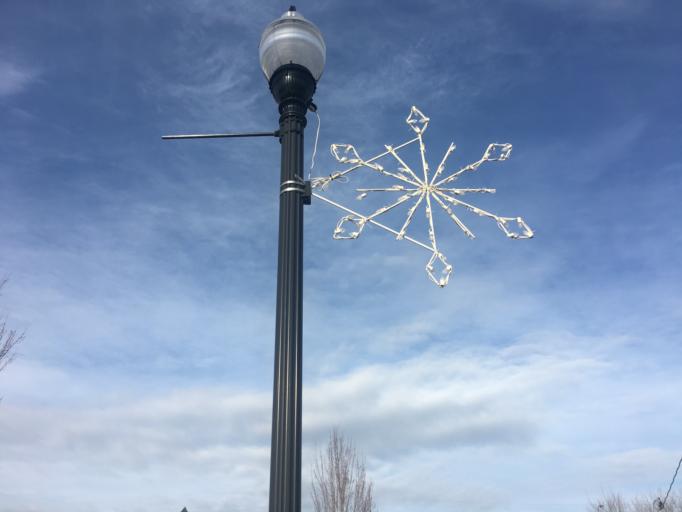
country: US
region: Oregon
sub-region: Washington County
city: Hillsboro
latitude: 45.5202
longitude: -122.9880
